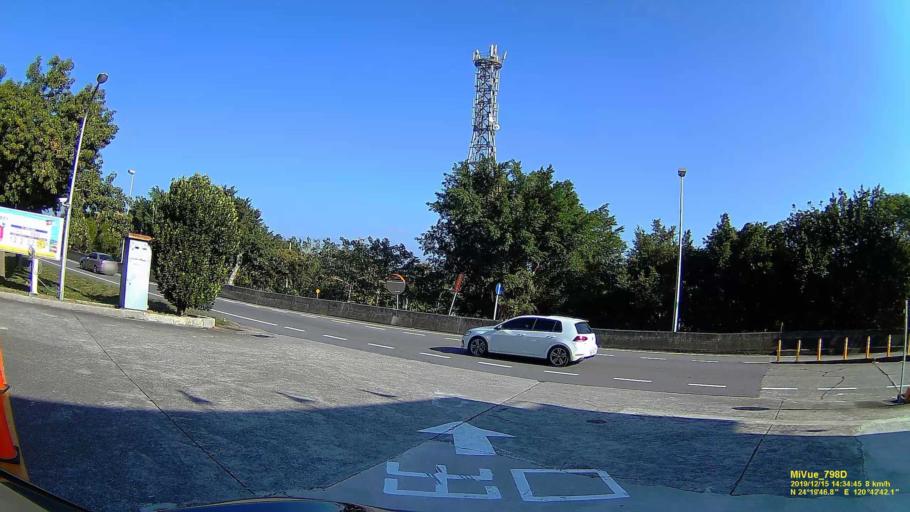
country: TW
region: Taiwan
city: Fengyuan
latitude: 24.3297
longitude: 120.7118
